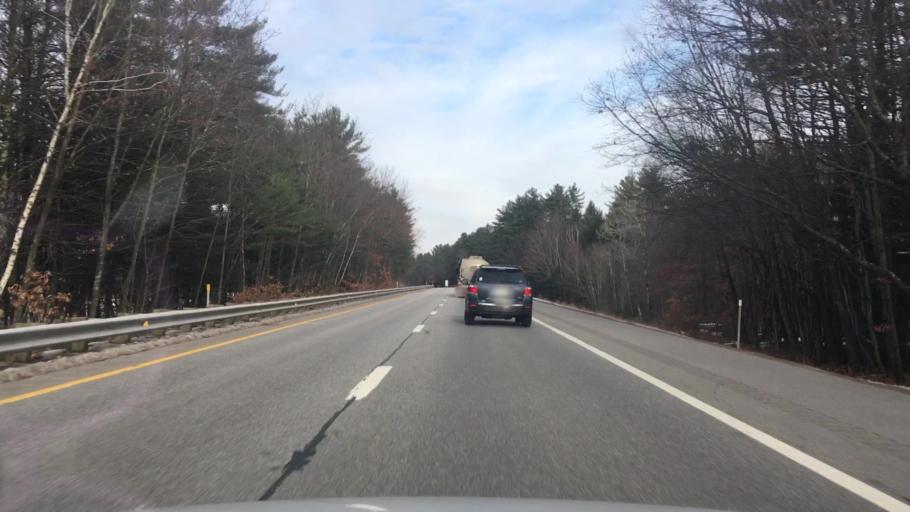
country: US
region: New Hampshire
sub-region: Merrimack County
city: Contoocook
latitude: 43.2089
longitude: -71.7122
